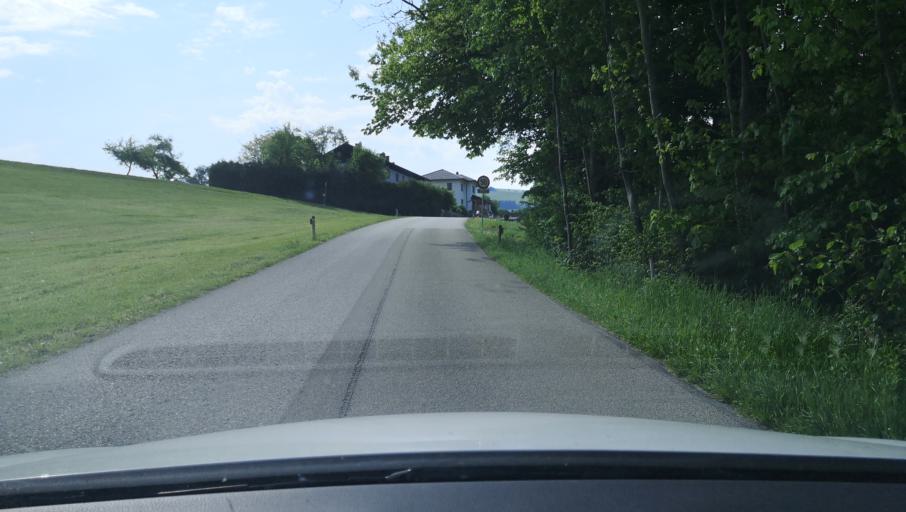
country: AT
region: Lower Austria
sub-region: Politischer Bezirk Amstetten
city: Neuhofen an der Ybbs
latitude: 48.0508
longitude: 14.8822
